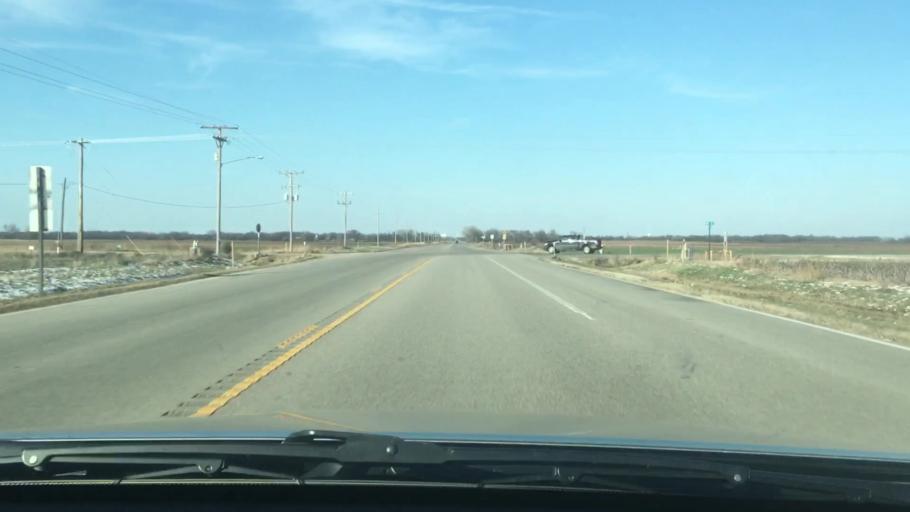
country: US
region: Kansas
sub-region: Rice County
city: Lyons
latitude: 38.2889
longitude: -98.2018
